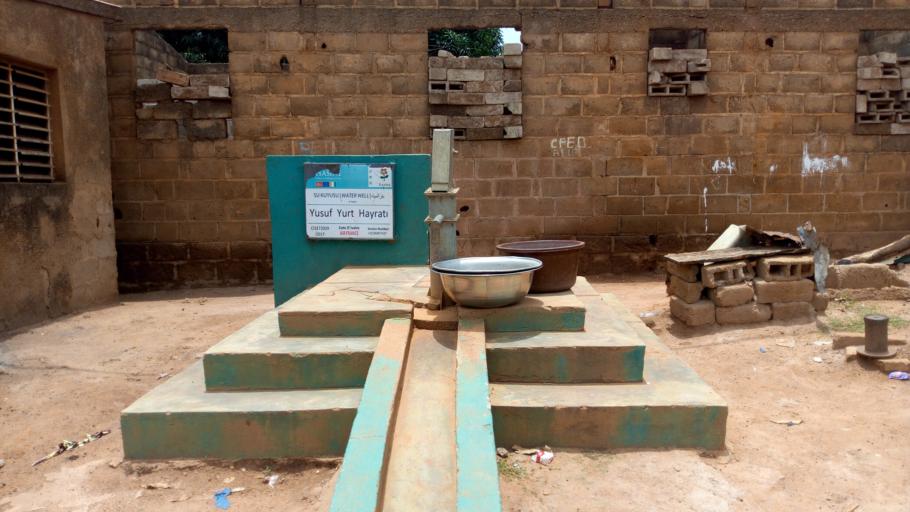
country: CI
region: Vallee du Bandama
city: Bouake
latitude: 7.7236
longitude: -5.0245
